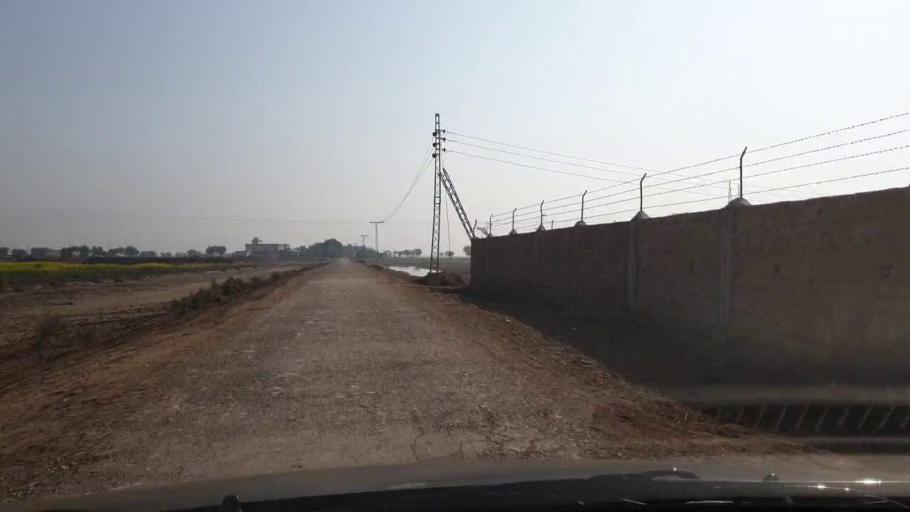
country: PK
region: Sindh
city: Sanghar
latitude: 25.9772
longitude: 68.9718
